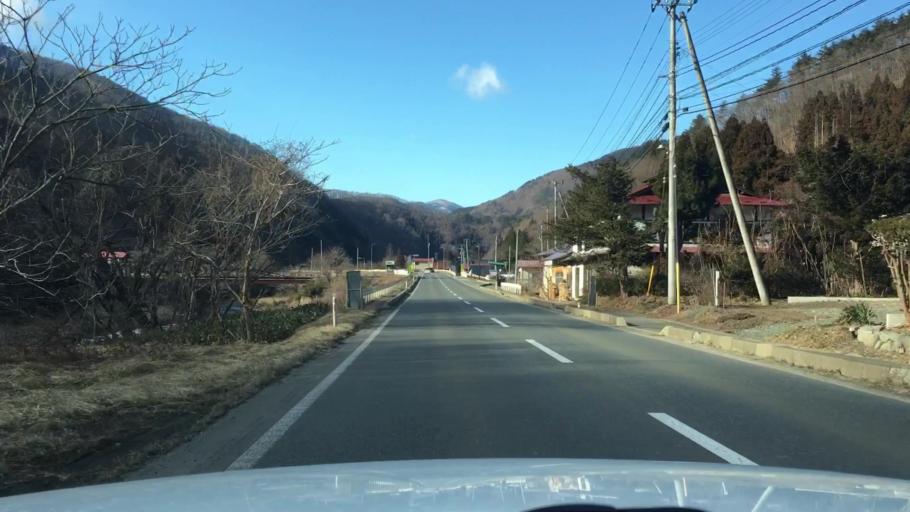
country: JP
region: Iwate
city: Tono
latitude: 39.6129
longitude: 141.6295
